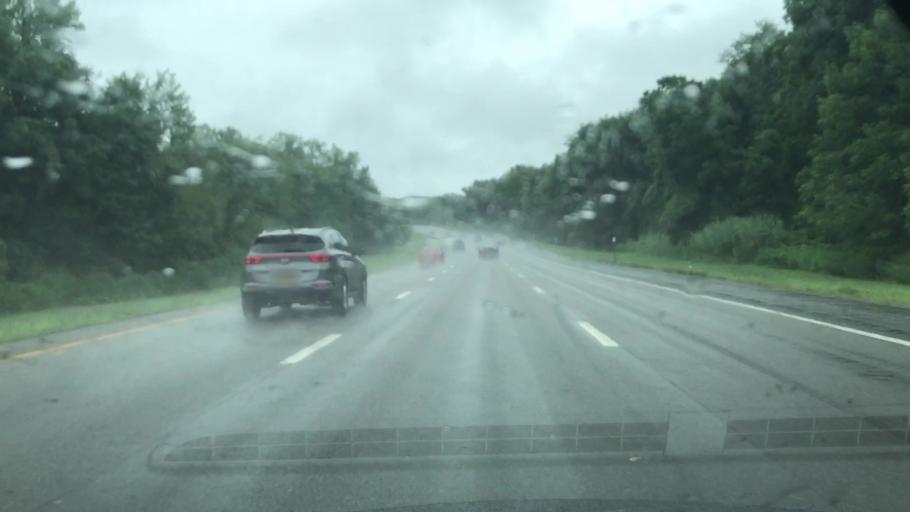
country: US
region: New York
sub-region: Westchester County
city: Briarcliff Manor
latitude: 41.2091
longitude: -73.8094
